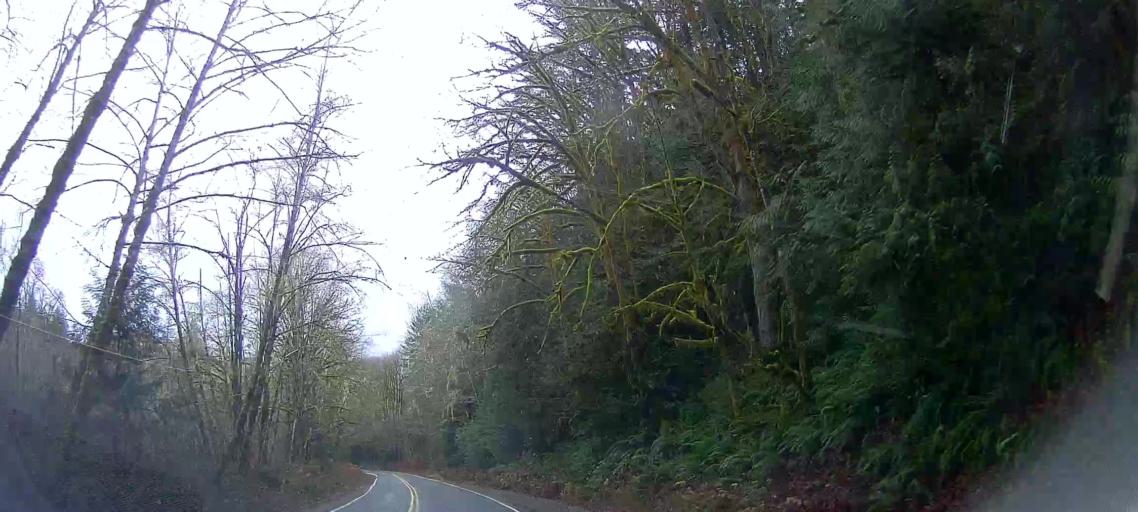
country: US
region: Washington
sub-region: Snohomish County
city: Darrington
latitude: 48.4853
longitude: -121.4886
